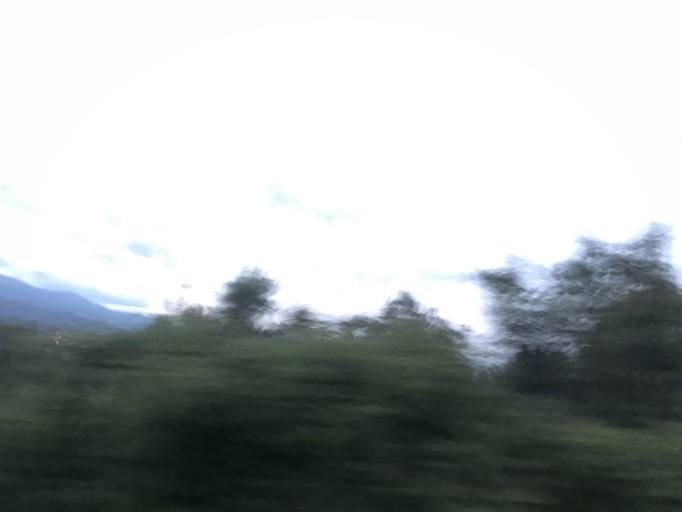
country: TR
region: Hatay
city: Uzunbag
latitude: 36.1275
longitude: 36.0406
